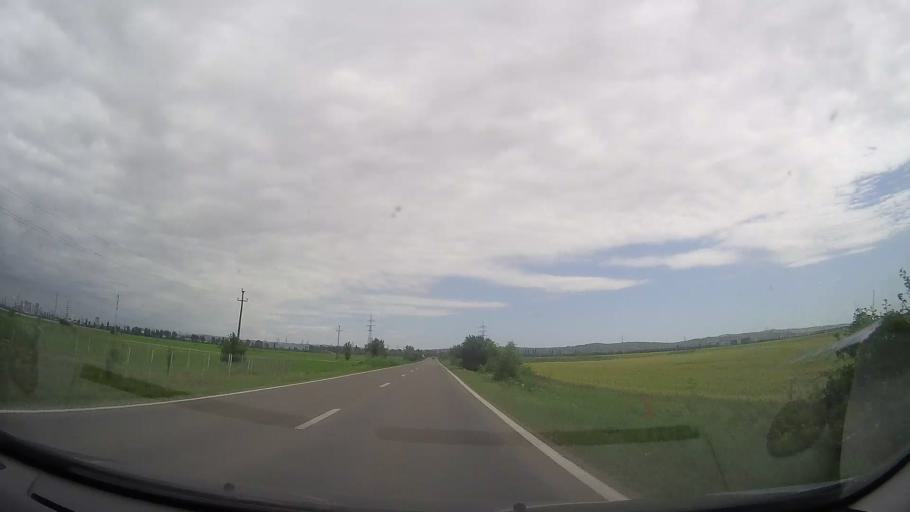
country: RO
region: Prahova
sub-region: Comuna Berceni
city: Berceni
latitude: 44.9279
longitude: 26.1033
